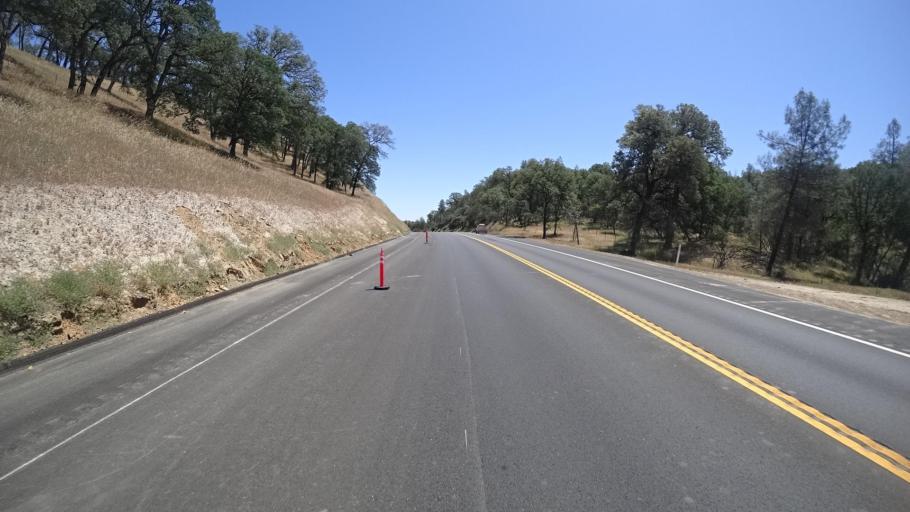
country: US
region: California
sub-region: Lake County
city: Hidden Valley Lake
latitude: 38.8415
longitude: -122.6039
